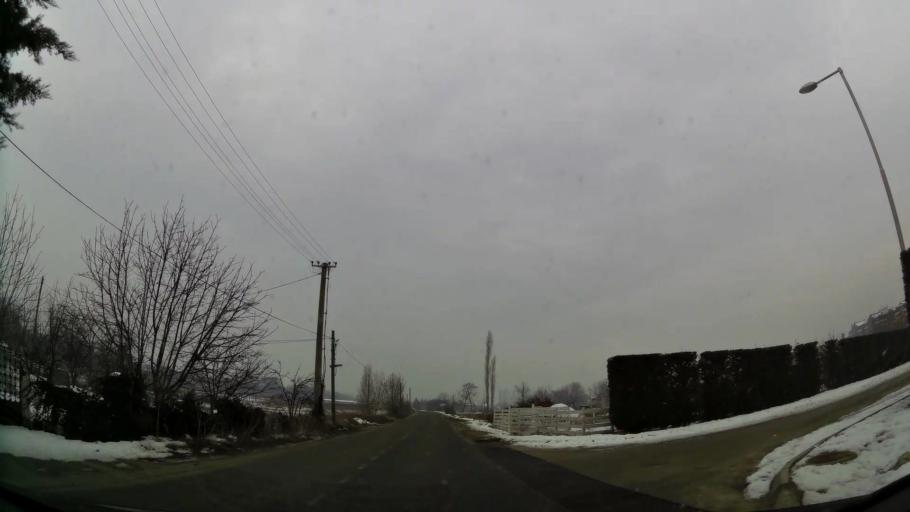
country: MK
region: Cucer-Sandevo
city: Chucher - Sandevo
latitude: 42.0515
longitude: 21.3648
